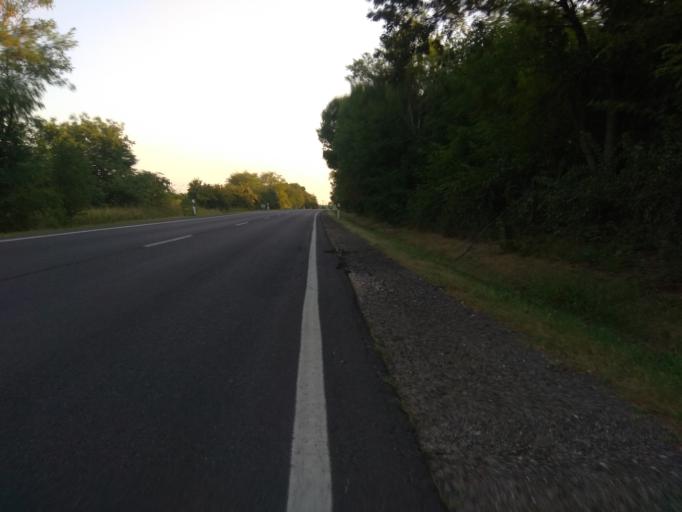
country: HU
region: Borsod-Abauj-Zemplen
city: Nyekladhaza
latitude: 47.9556
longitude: 20.8342
